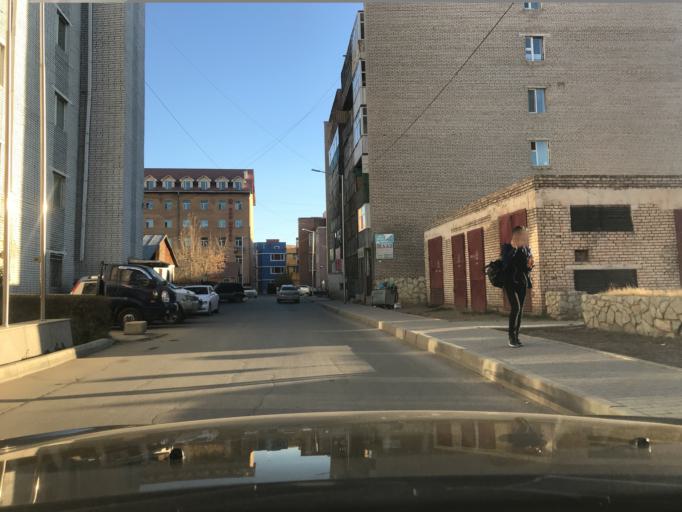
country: MN
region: Ulaanbaatar
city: Ulaanbaatar
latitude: 47.9276
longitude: 106.9110
